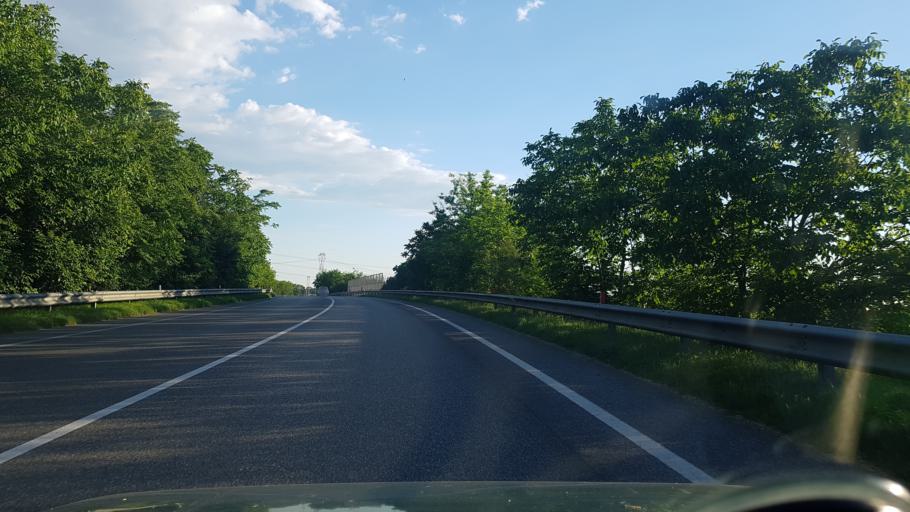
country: IT
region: Friuli Venezia Giulia
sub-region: Provincia di Gorizia
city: Villesse
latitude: 45.8587
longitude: 13.4301
